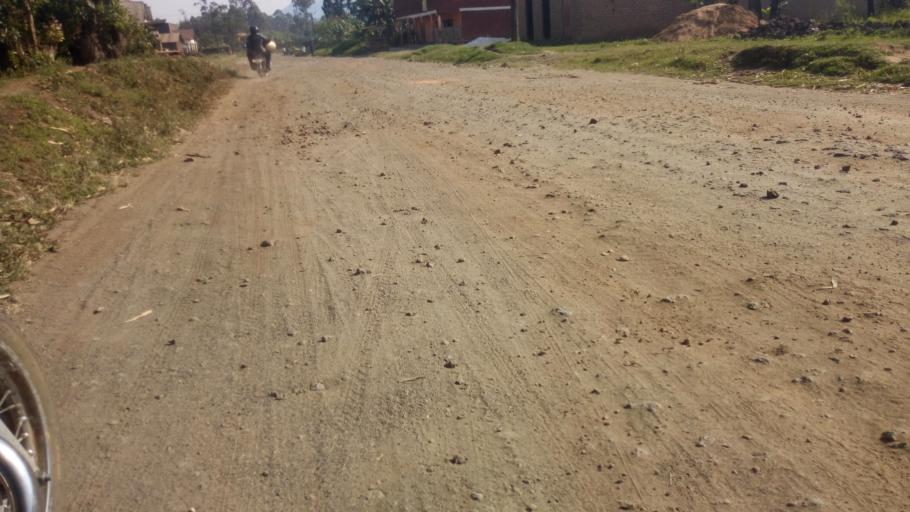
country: UG
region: Western Region
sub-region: Kisoro District
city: Kisoro
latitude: -1.2508
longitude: 29.7137
